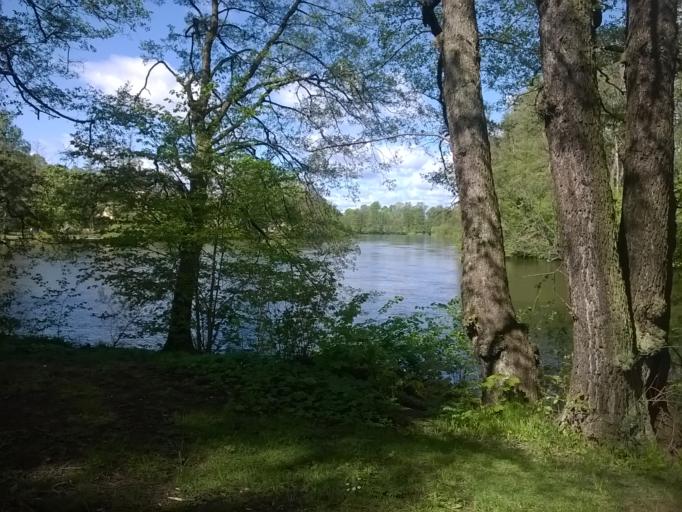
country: SE
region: OEstergoetland
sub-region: Norrkopings Kommun
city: Norrkoping
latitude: 58.5868
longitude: 16.1637
